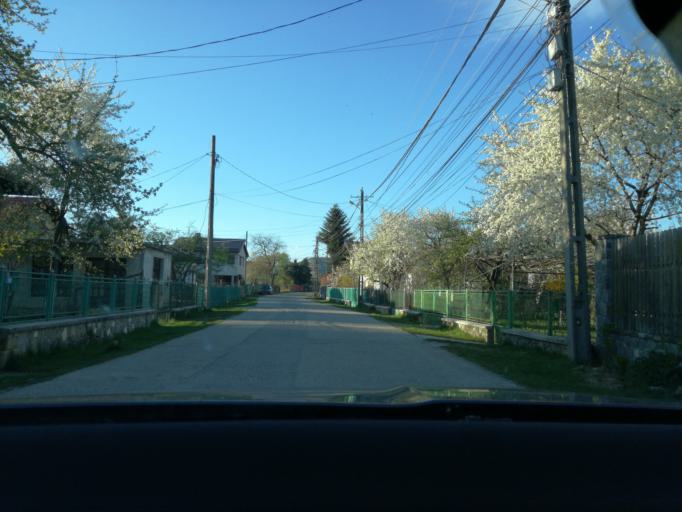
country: RO
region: Prahova
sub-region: Comuna Cornu
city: Cornu de Jos
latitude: 45.1486
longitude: 25.7018
